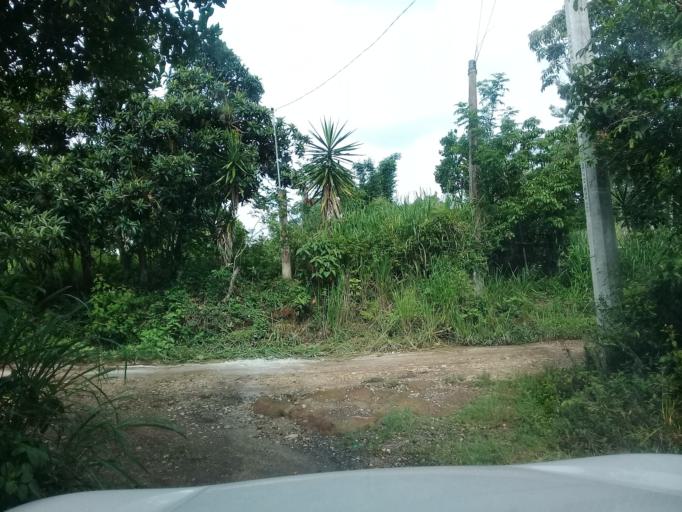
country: MX
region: Veracruz
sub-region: Emiliano Zapata
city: Jacarandas
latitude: 19.4818
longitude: -96.8529
